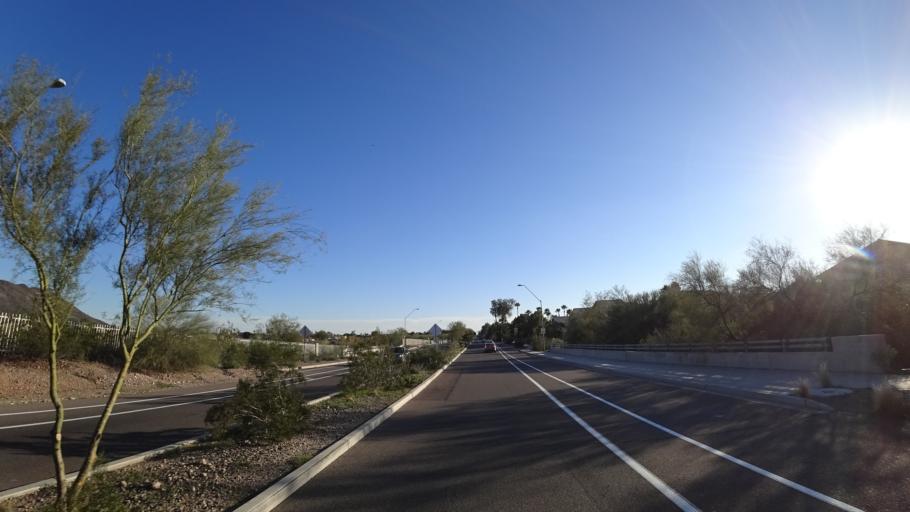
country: US
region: Arizona
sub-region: Maricopa County
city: Peoria
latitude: 33.6865
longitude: -112.1867
